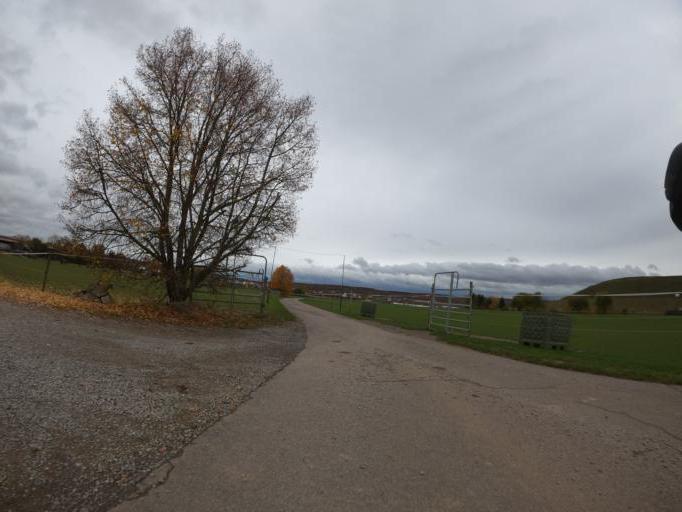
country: DE
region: Baden-Wuerttemberg
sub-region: Regierungsbezirk Stuttgart
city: Ehningen
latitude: 48.6662
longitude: 8.9330
